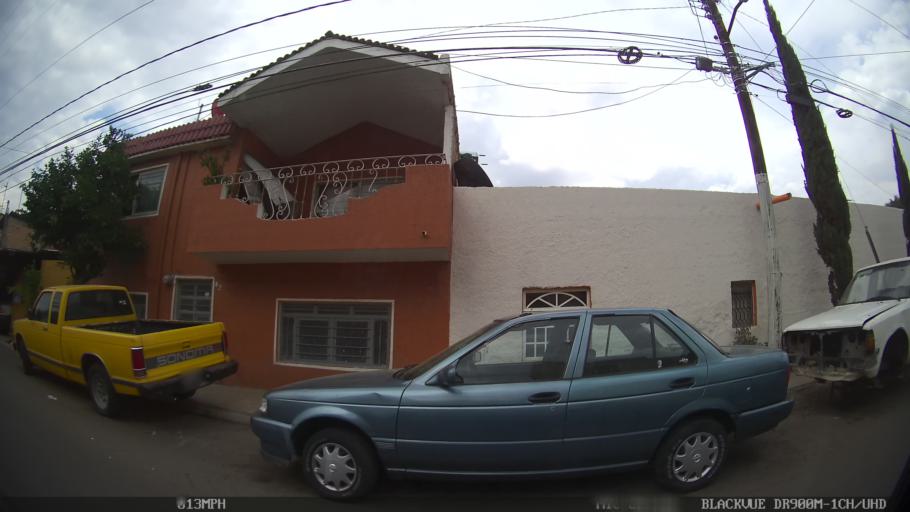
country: MX
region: Jalisco
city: Tlaquepaque
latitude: 20.6301
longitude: -103.2718
